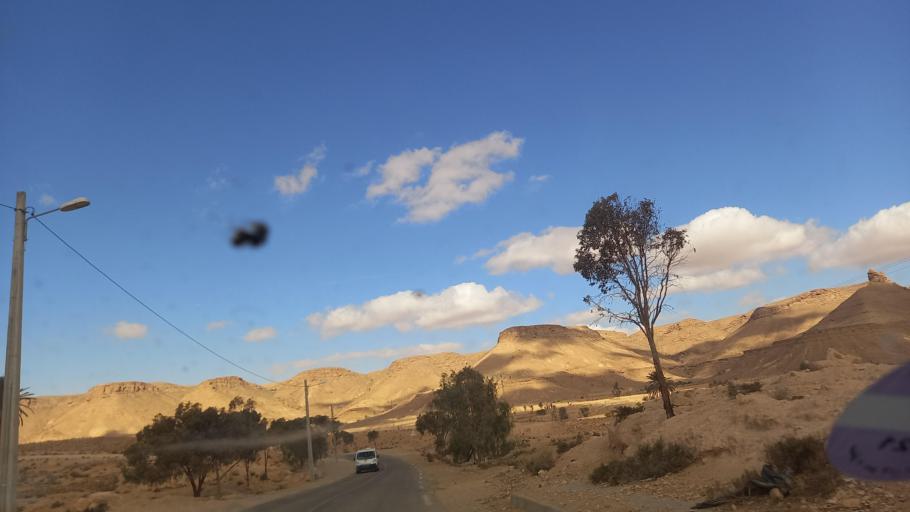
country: TN
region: Tataouine
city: Tataouine
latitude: 32.9154
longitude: 10.2772
